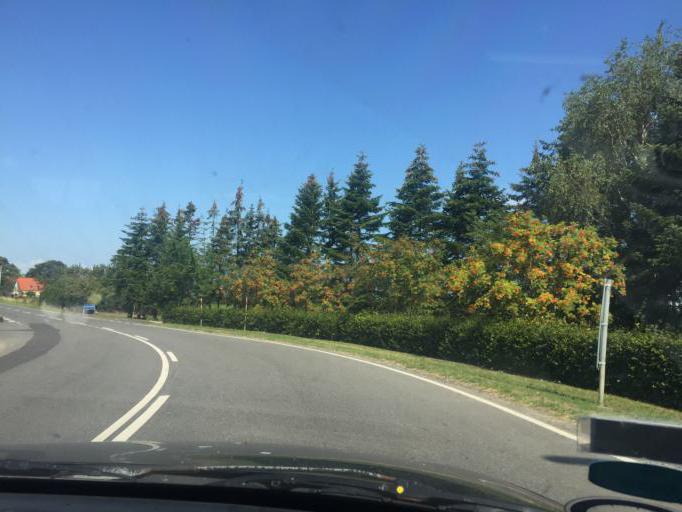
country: DK
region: Zealand
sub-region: Guldborgsund Kommune
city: Sakskobing
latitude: 54.7916
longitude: 11.5771
